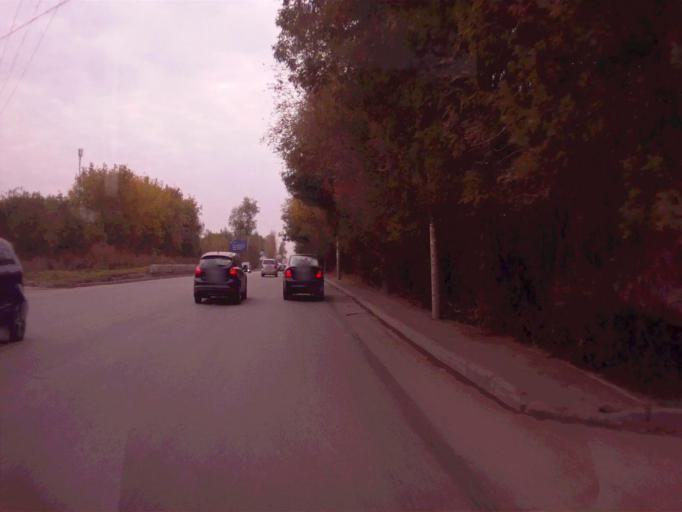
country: RU
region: Chelyabinsk
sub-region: Gorod Chelyabinsk
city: Chelyabinsk
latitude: 55.1284
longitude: 61.3854
